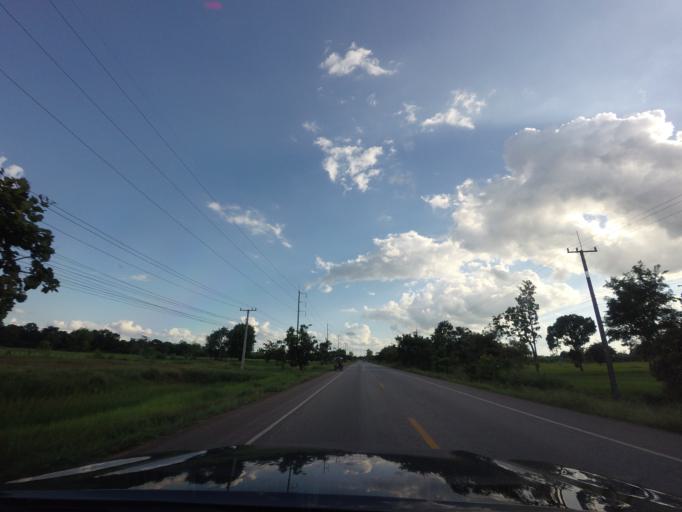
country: TH
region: Changwat Udon Thani
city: Thung Fon
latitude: 17.4730
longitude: 103.1938
